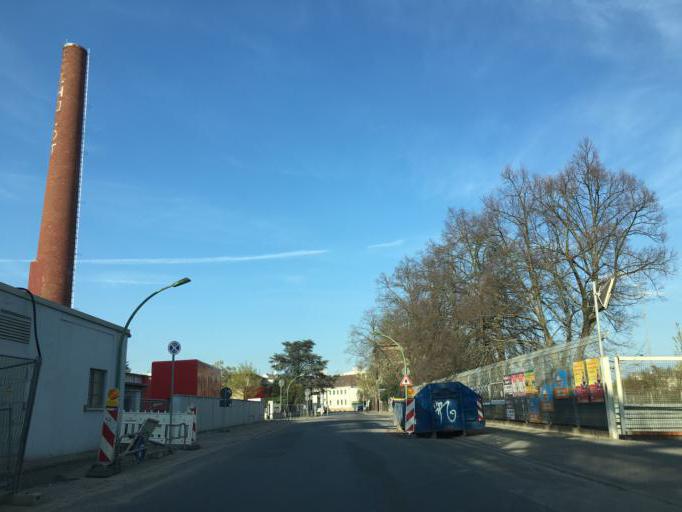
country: DE
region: Hesse
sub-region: Regierungsbezirk Darmstadt
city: Offenbach
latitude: 50.1184
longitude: 8.7384
